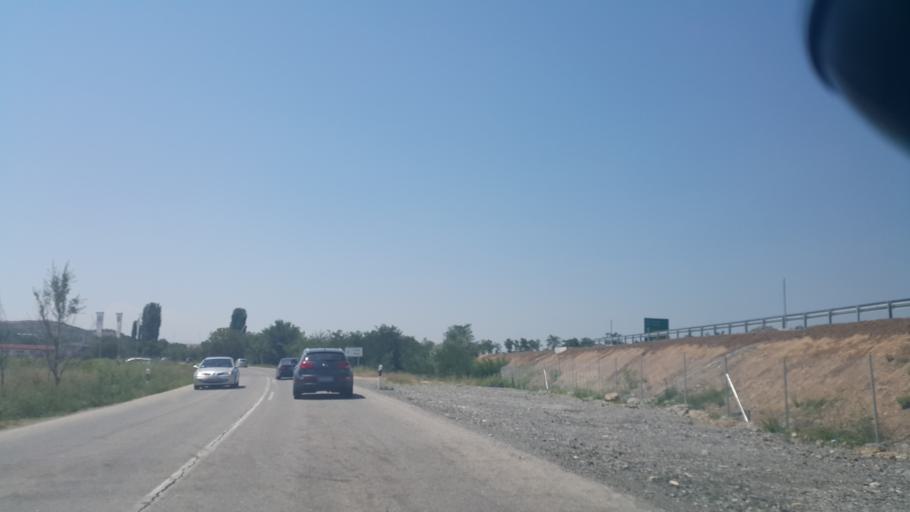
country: MK
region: Demir Kapija
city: Demir Kapija
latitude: 41.4130
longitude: 22.2442
